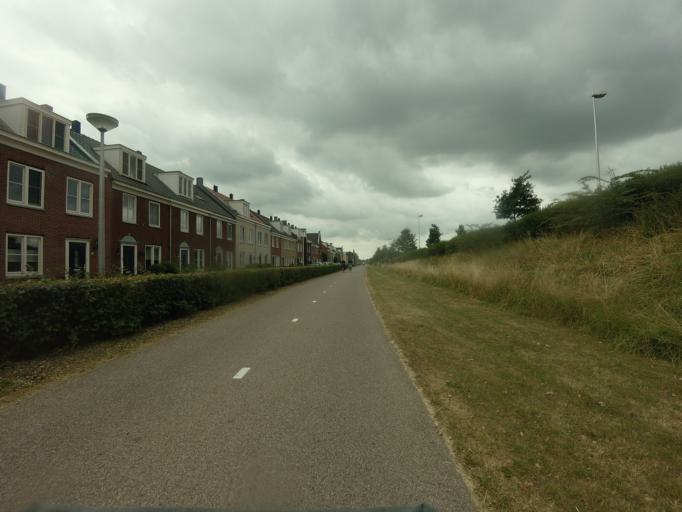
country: NL
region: Utrecht
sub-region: Stichtse Vecht
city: Spechtenkamp
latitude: 52.0989
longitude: 5.0144
